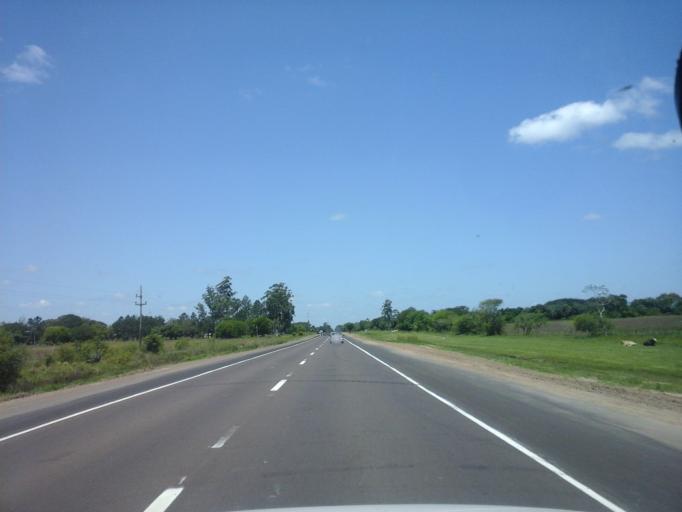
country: AR
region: Corrientes
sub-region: Departamento de Itati
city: Itati
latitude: -27.3670
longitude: -58.3511
